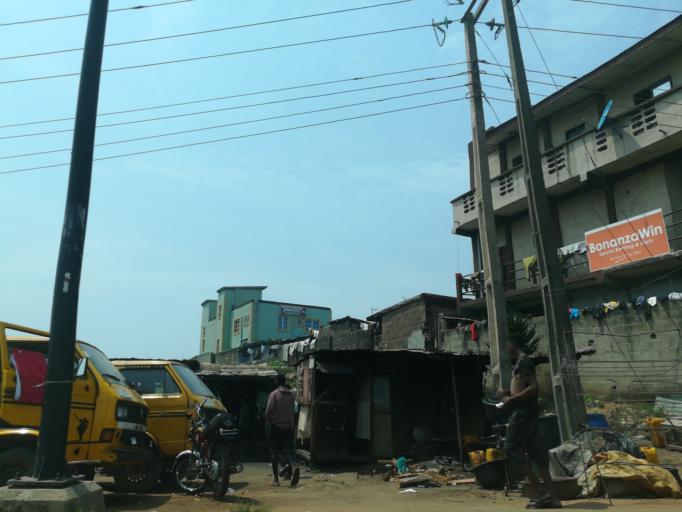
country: NG
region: Lagos
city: Ikorodu
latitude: 6.6256
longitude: 3.4853
